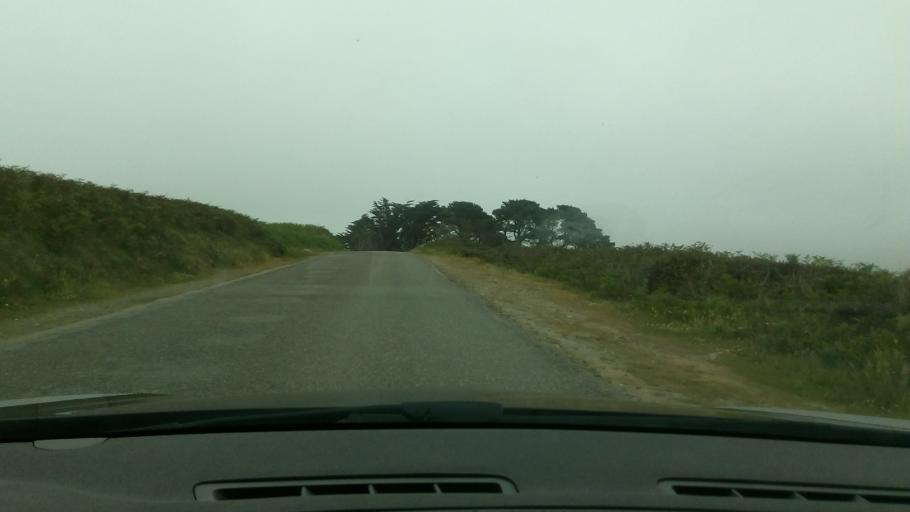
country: FR
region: Brittany
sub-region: Departement du Finistere
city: Le Conquet
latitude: 48.3640
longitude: -4.7743
